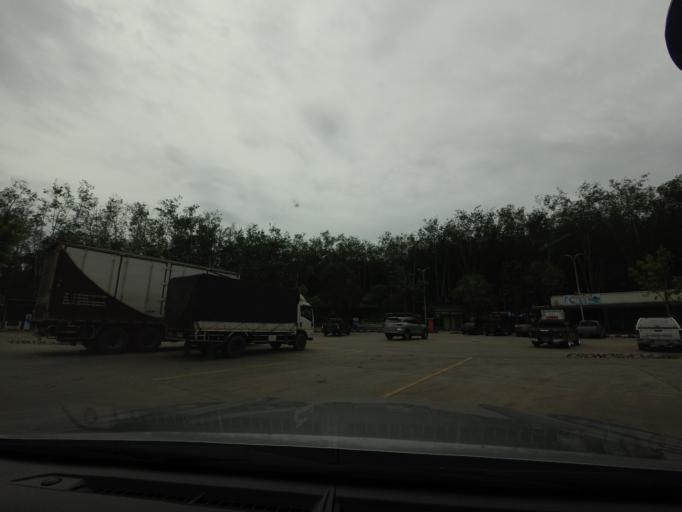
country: TH
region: Prachuap Khiri Khan
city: Bang Saphan Noi
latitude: 10.9303
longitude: 99.2894
